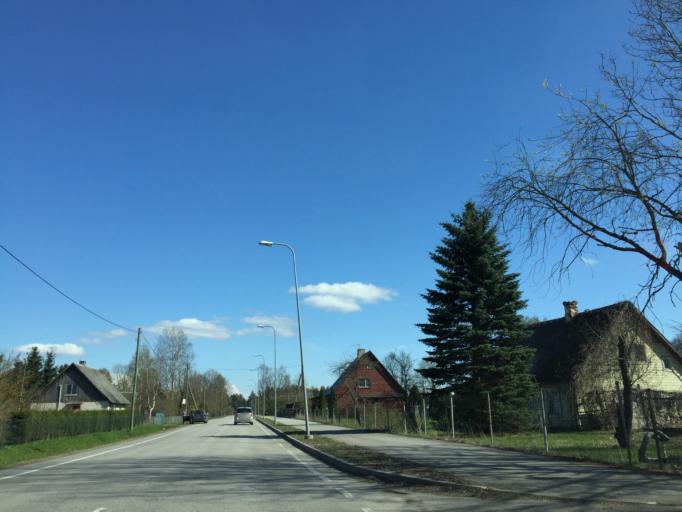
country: EE
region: Valgamaa
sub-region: Valga linn
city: Valga
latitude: 57.8637
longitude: 26.1980
